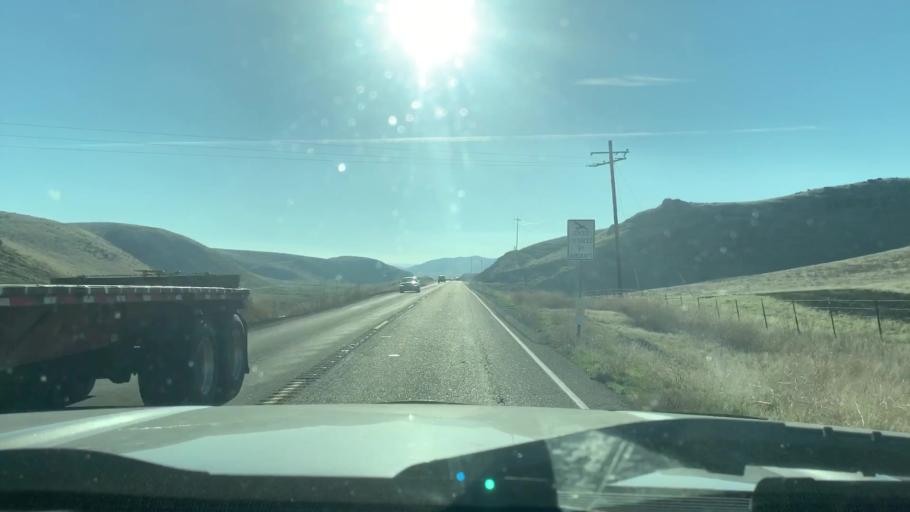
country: US
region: California
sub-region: San Luis Obispo County
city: Shandon
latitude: 35.7584
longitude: -120.2587
